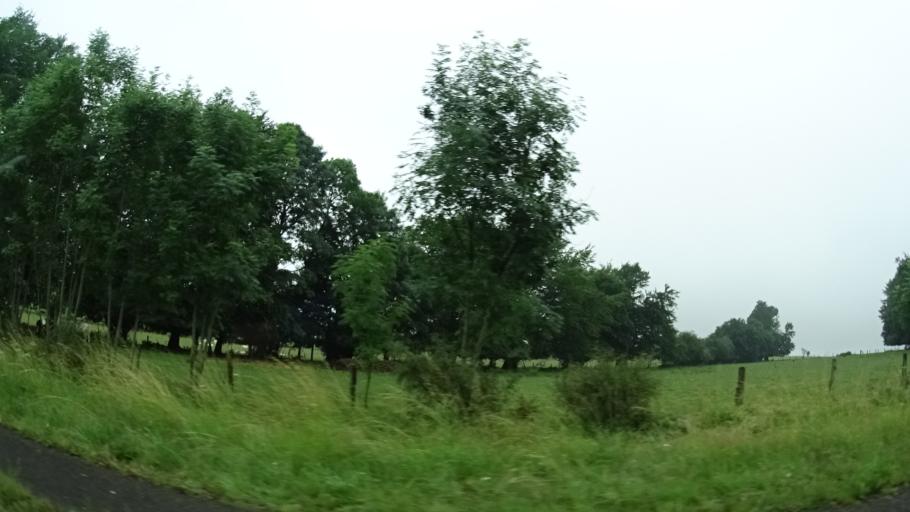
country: BE
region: Wallonia
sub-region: Province du Luxembourg
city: Neufchateau
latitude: 49.8973
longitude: 5.3821
